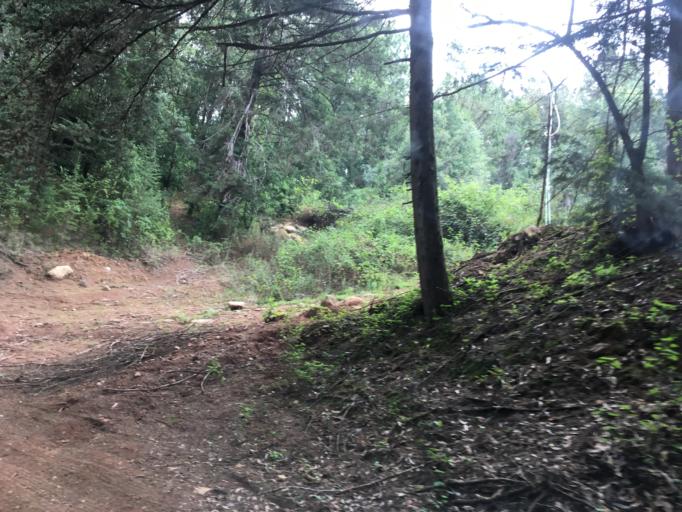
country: MX
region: Michoacan
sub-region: Zitacuaro
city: La Fundicion (Quinta Manzana)
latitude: 19.4966
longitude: -100.3112
